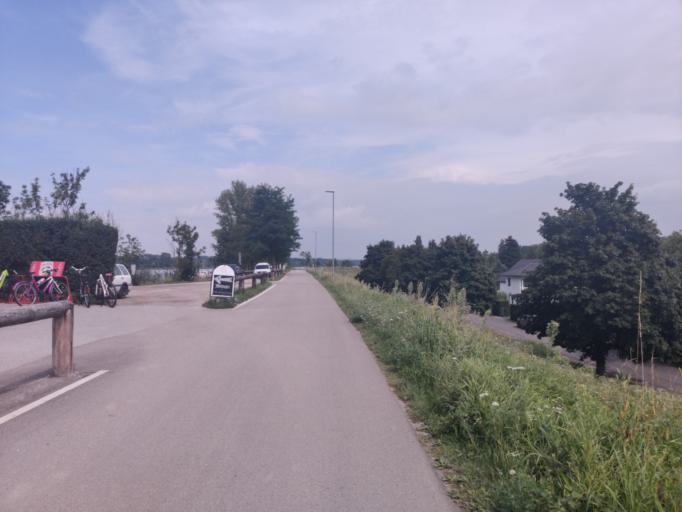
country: AT
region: Lower Austria
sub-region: Politischer Bezirk Tulln
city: Konigstetten
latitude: 48.3366
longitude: 16.1604
